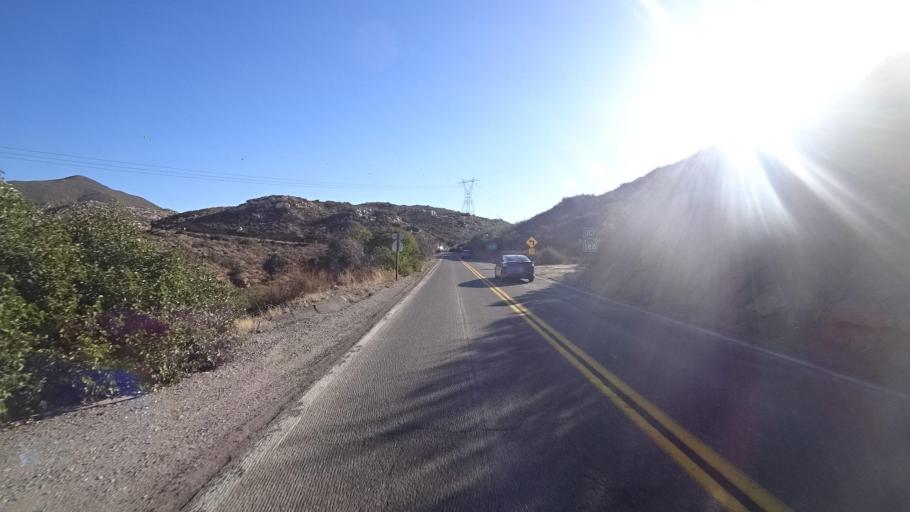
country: MX
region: Baja California
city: Tecate
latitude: 32.5974
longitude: -116.6450
